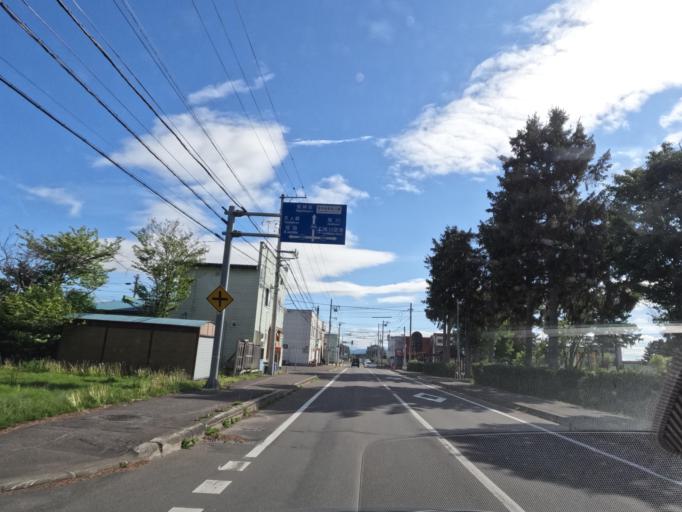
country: JP
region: Hokkaido
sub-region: Asahikawa-shi
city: Asahikawa
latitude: 43.6982
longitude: 142.5084
